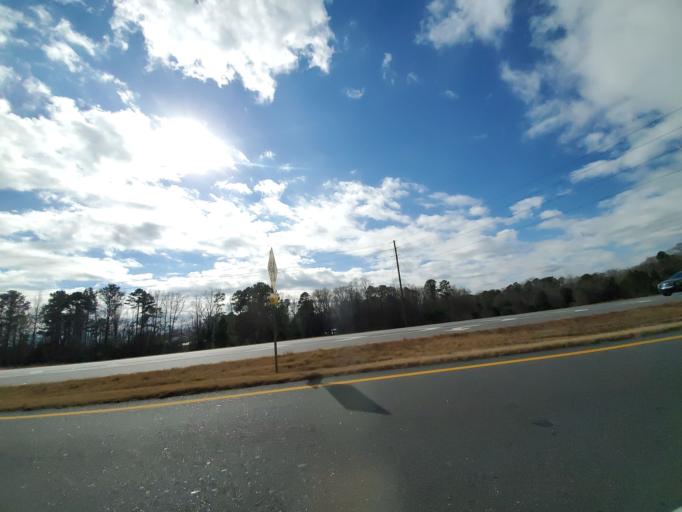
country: US
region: Georgia
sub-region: Clarke County
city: Country Club Estates
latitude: 33.9997
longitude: -83.4449
